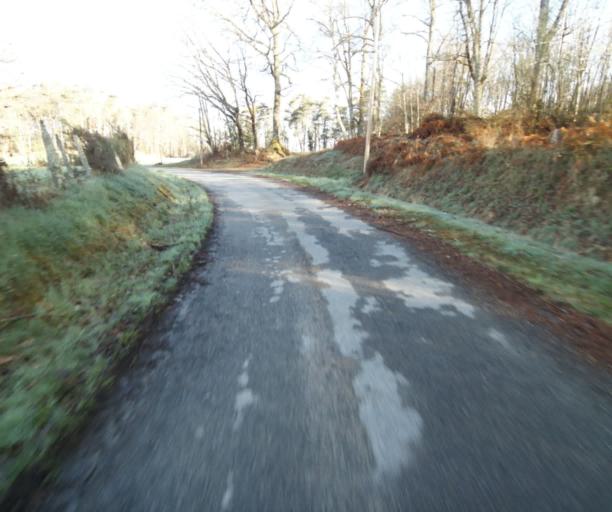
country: FR
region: Limousin
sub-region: Departement de la Correze
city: Correze
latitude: 45.2889
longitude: 1.8637
